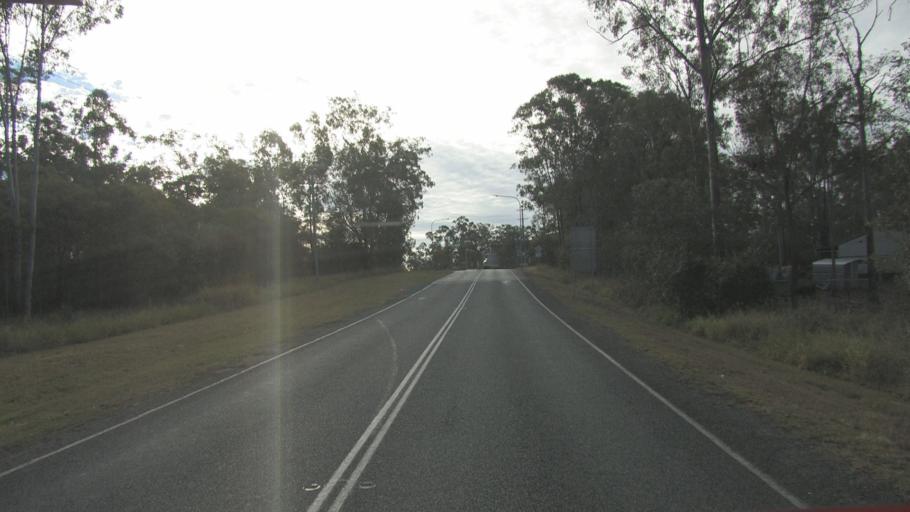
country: AU
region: Queensland
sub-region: Logan
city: Cedar Vale
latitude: -27.8371
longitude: 153.0466
